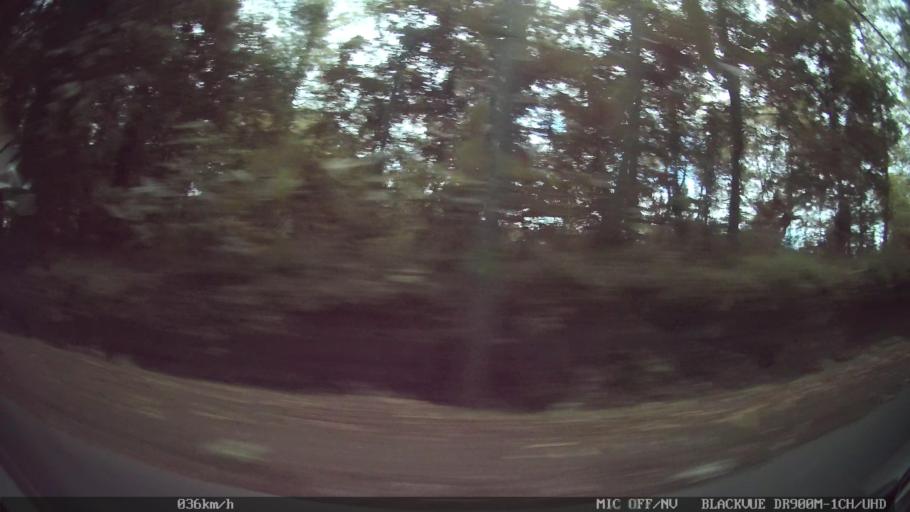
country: ID
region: Bali
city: Banjar Kedisan
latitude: -8.2601
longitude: 115.3355
